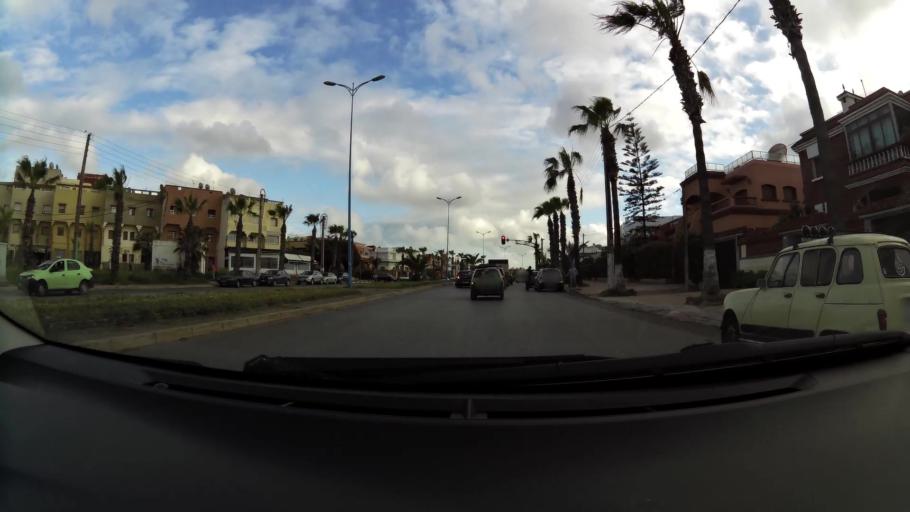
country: MA
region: Grand Casablanca
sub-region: Mohammedia
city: Mohammedia
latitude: 33.6998
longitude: -7.3707
